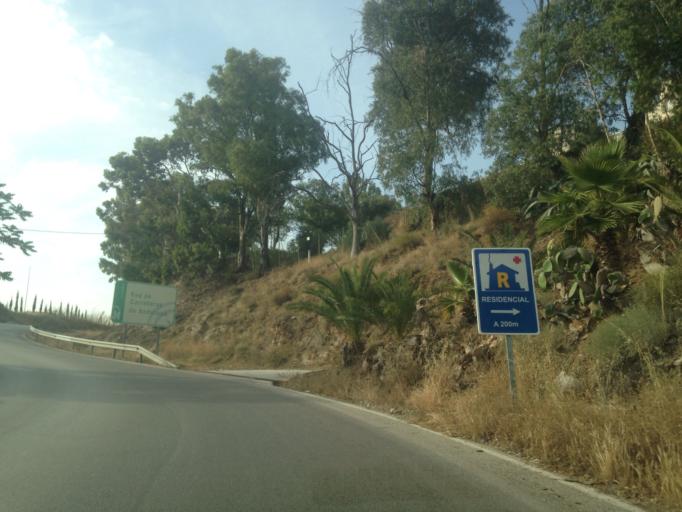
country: ES
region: Andalusia
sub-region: Provincia de Malaga
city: Malaga
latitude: 36.7471
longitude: -4.4076
